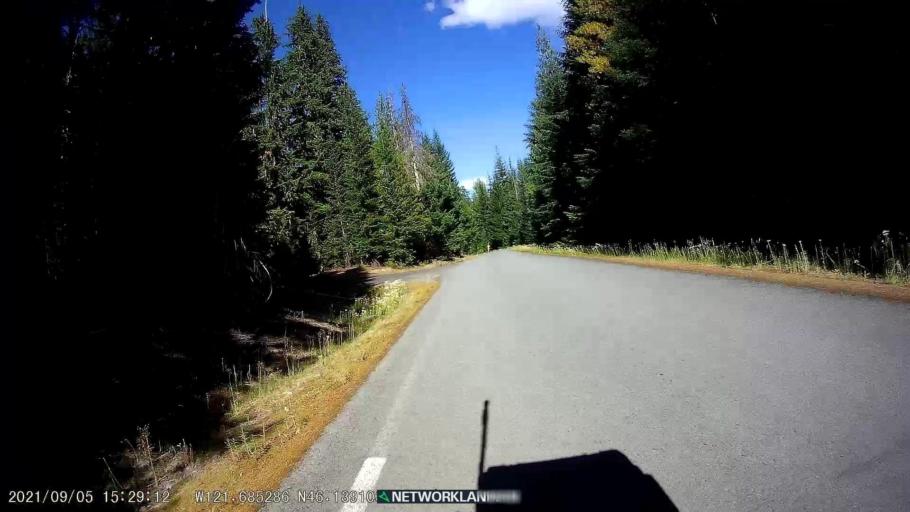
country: US
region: Washington
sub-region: Skamania County
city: Carson
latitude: 46.1389
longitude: -121.6856
